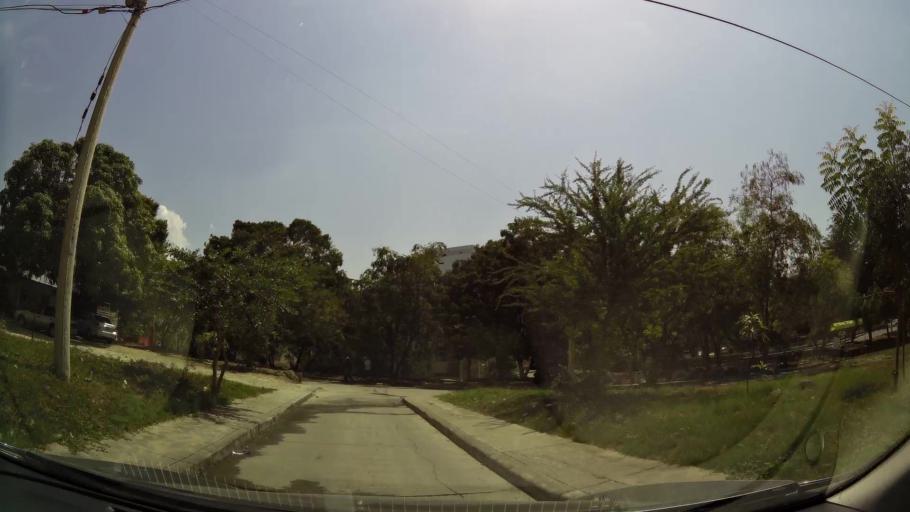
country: CO
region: Bolivar
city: Cartagena
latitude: 10.3979
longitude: -75.4894
